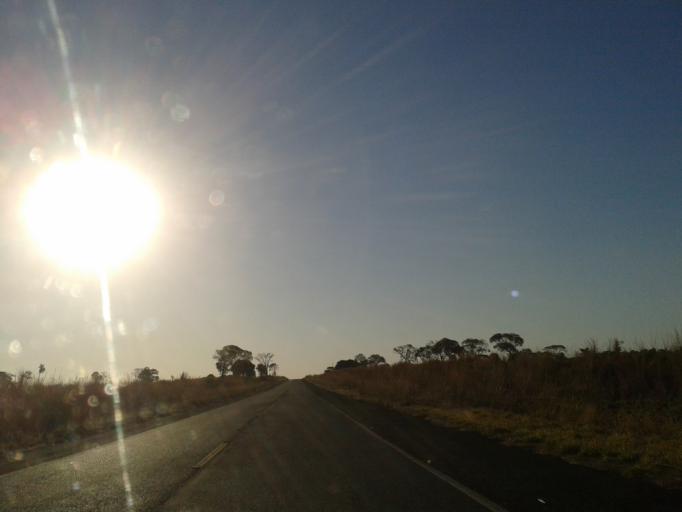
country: BR
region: Minas Gerais
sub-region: Santa Vitoria
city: Santa Vitoria
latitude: -19.0951
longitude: -50.3392
